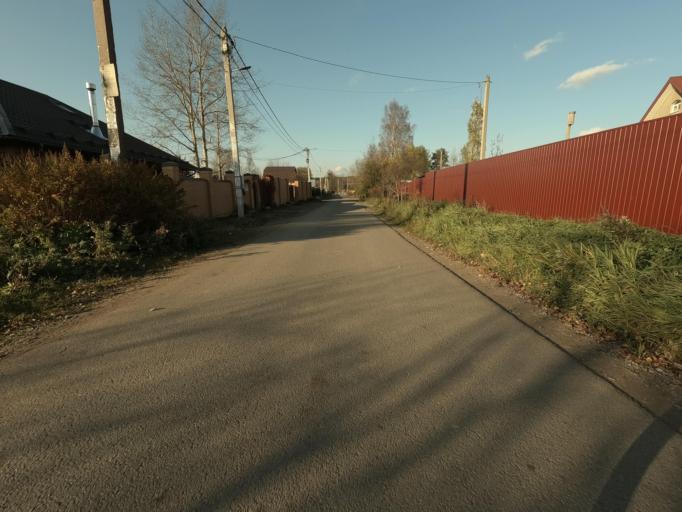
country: RU
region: Leningrad
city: Luppolovo
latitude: 60.1365
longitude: 30.2562
